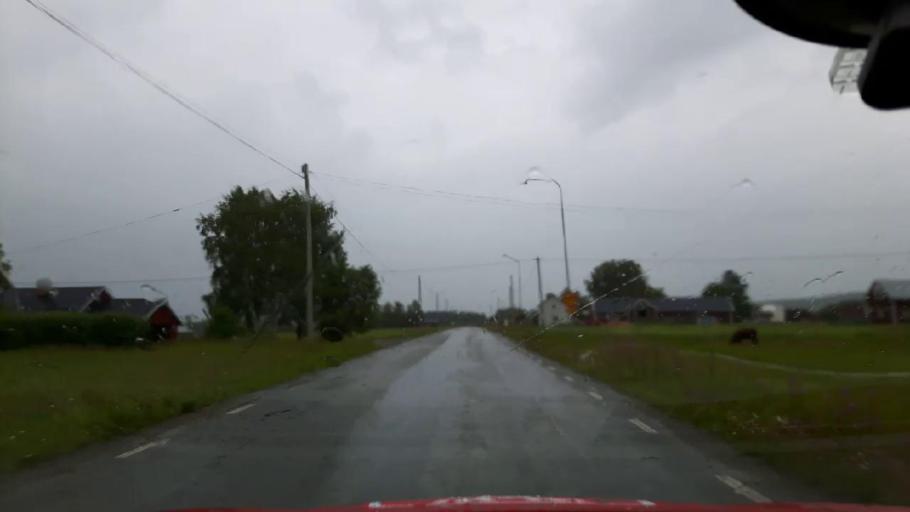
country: SE
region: Jaemtland
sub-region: OEstersunds Kommun
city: Brunflo
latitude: 62.9874
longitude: 14.8092
